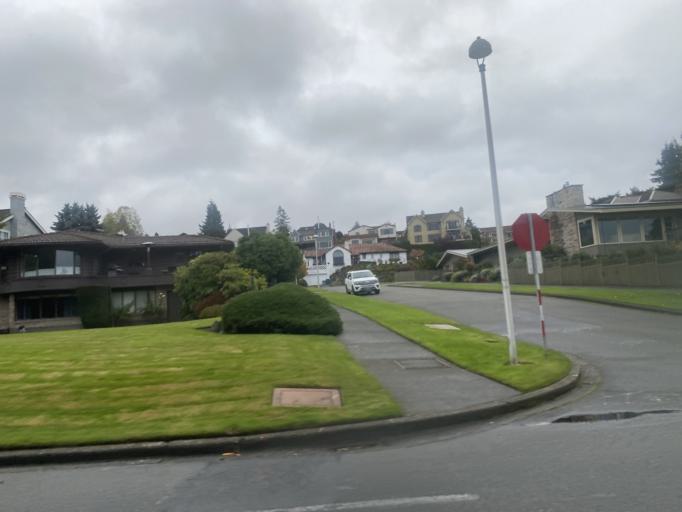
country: US
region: Washington
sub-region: King County
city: Seattle
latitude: 47.6457
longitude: -122.4143
